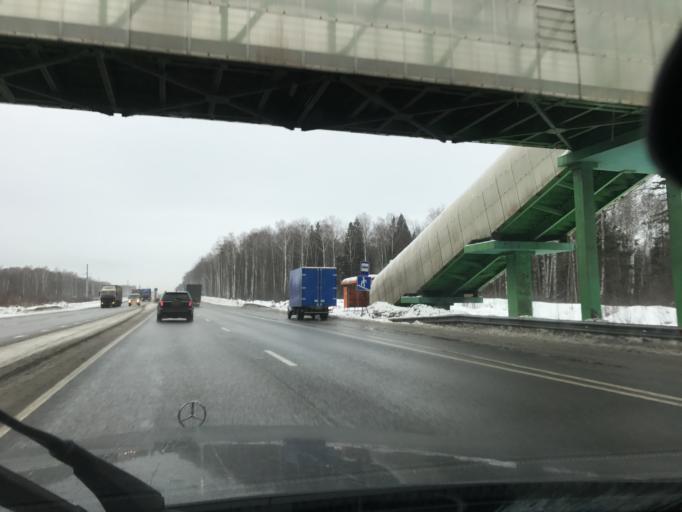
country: RU
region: Nizjnij Novgorod
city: Smolino
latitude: 56.2816
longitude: 43.0919
